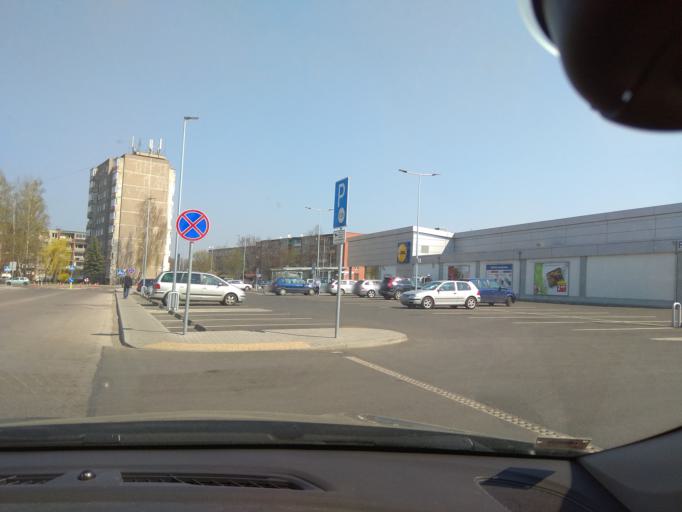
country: LT
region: Marijampoles apskritis
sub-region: Marijampole Municipality
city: Marijampole
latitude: 54.5667
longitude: 23.3477
